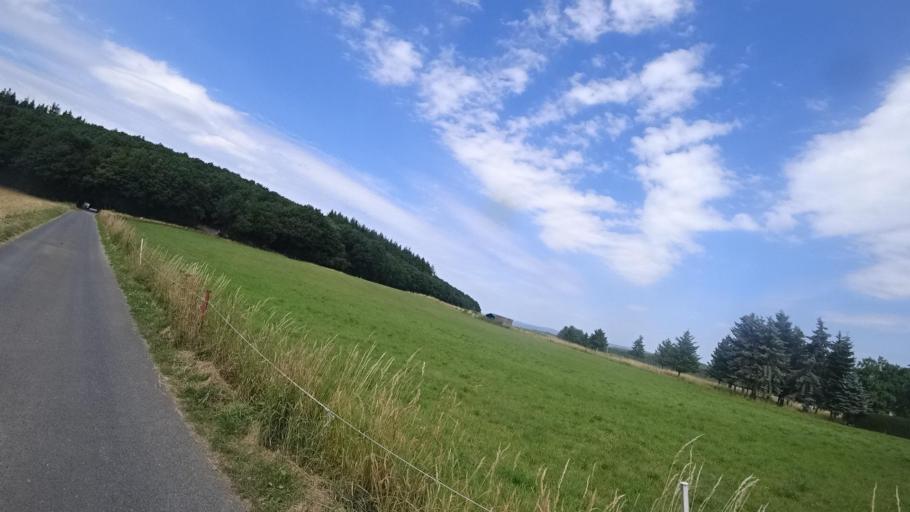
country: DE
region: Rheinland-Pfalz
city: Spessart
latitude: 50.4915
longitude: 7.0930
